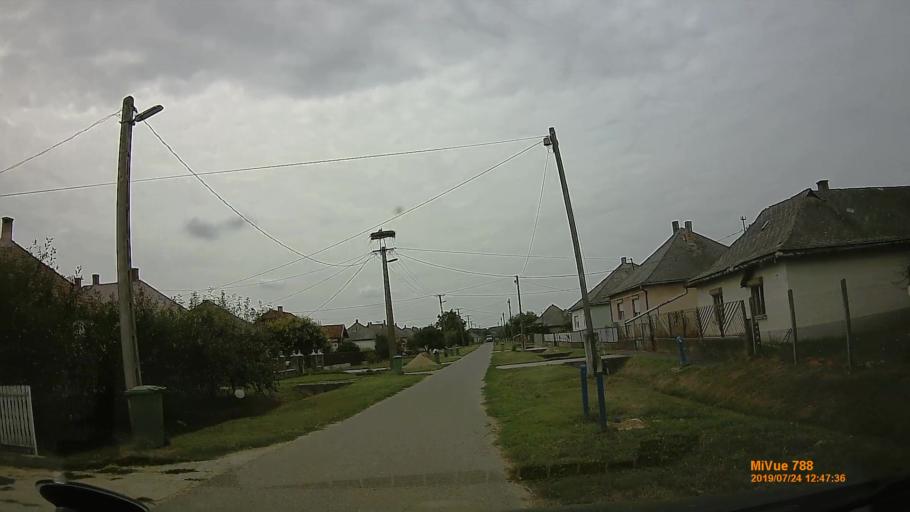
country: HU
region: Szabolcs-Szatmar-Bereg
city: Aranyosapati
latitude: 48.1927
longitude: 22.3162
